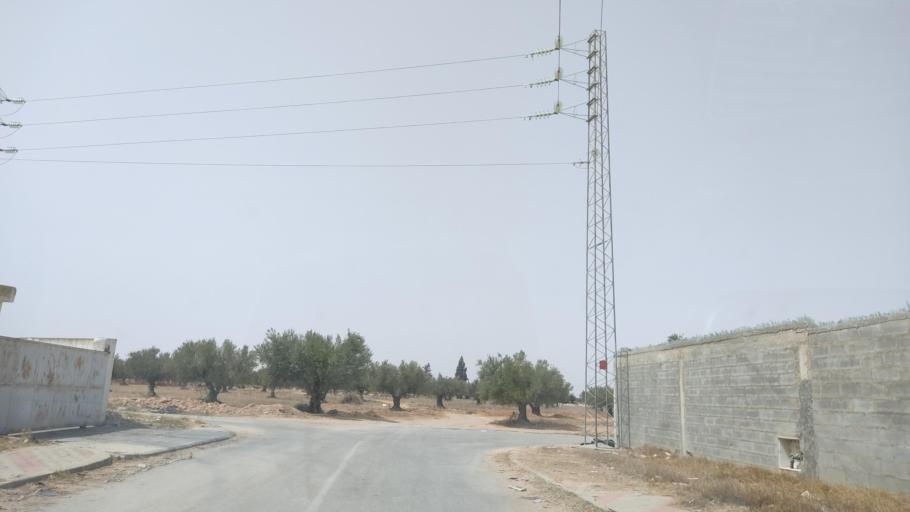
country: TN
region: Al Mahdiyah
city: El Jem
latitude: 35.1285
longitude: 10.7360
